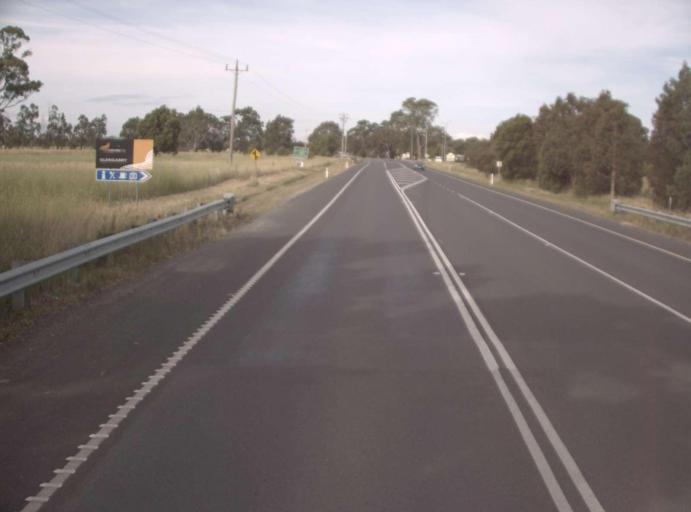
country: AU
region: Victoria
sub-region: Latrobe
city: Traralgon
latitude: -38.1304
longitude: 146.5611
